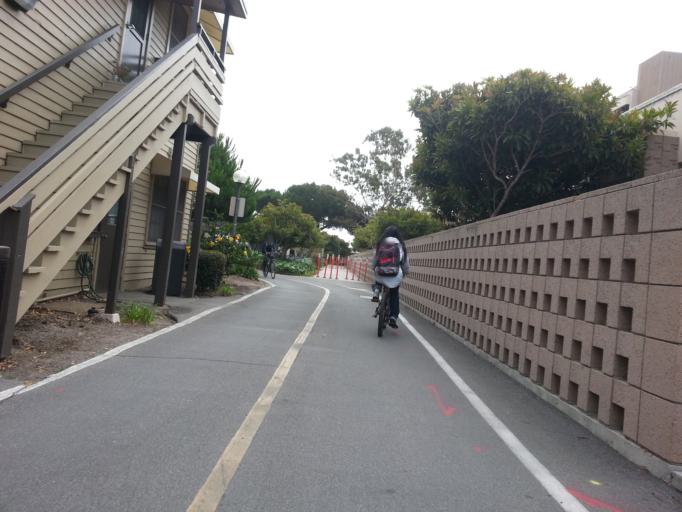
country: US
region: California
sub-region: Santa Barbara County
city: Isla Vista
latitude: 34.4167
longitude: -119.8449
